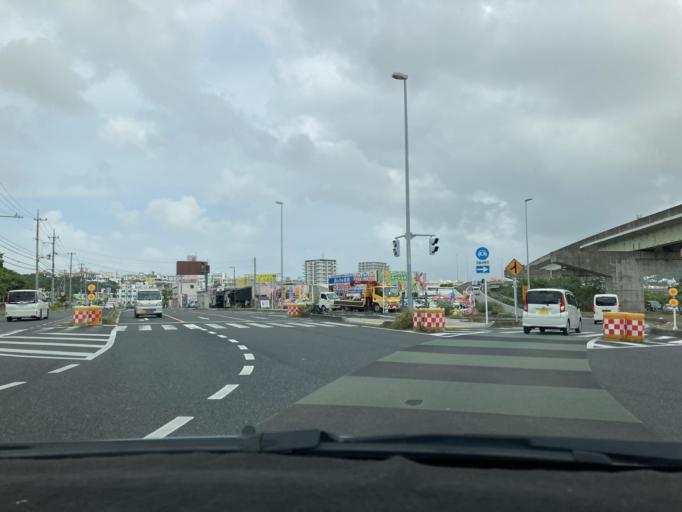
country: JP
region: Okinawa
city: Tomigusuku
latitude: 26.1759
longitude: 127.6684
